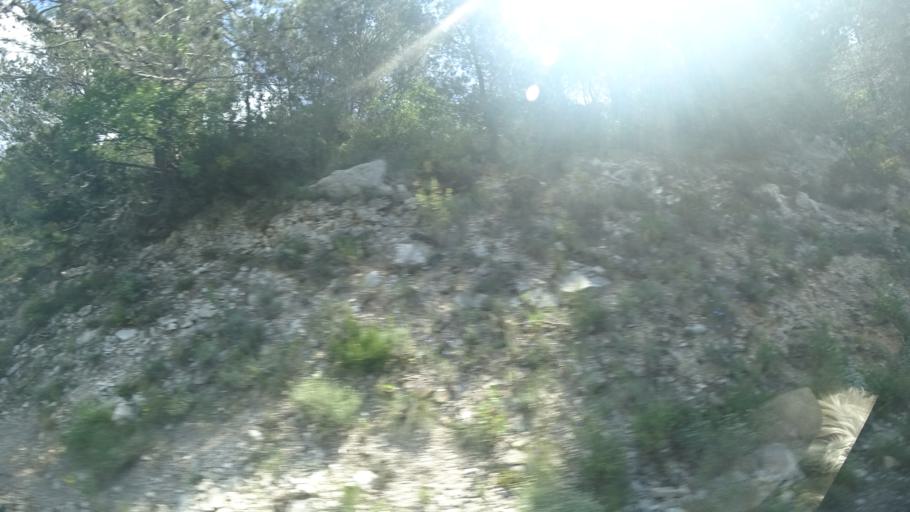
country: FR
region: Languedoc-Roussillon
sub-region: Departement de l'Herault
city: Olonzac
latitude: 43.3516
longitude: 2.7566
